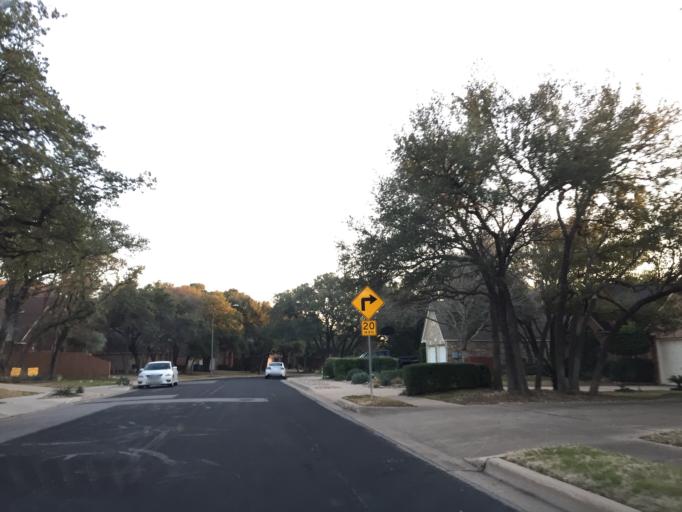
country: US
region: Texas
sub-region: Williamson County
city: Jollyville
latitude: 30.4213
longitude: -97.7568
